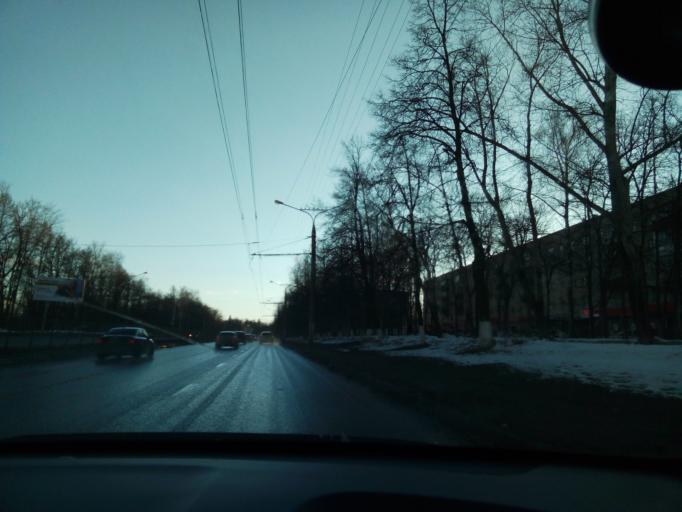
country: RU
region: Chuvashia
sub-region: Cheboksarskiy Rayon
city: Cheboksary
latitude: 56.1401
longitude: 47.1958
